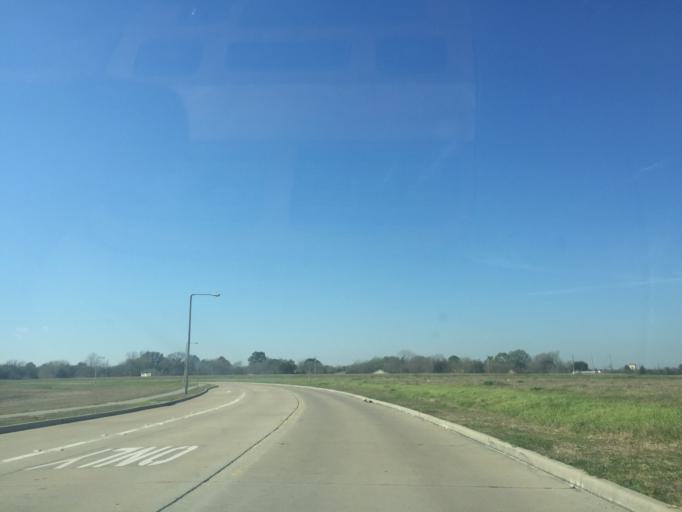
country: US
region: Texas
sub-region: Galveston County
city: Kemah
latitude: 29.5134
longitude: -95.0274
